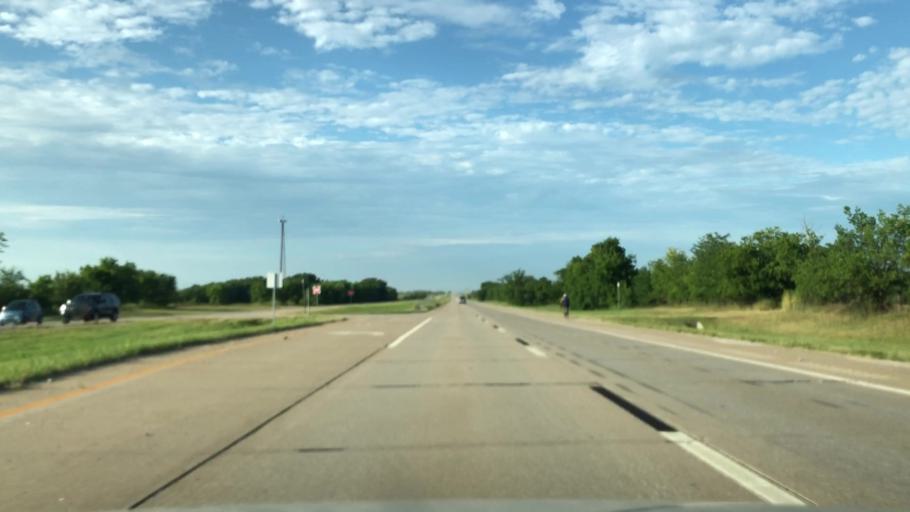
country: US
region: Oklahoma
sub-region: Osage County
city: Skiatook
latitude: 36.4025
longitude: -95.9206
